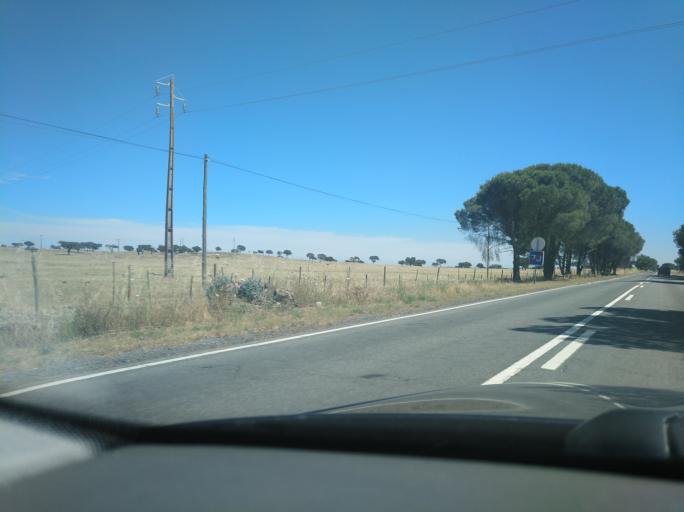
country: PT
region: Beja
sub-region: Almodovar
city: Almodovar
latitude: 37.5766
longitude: -8.0764
